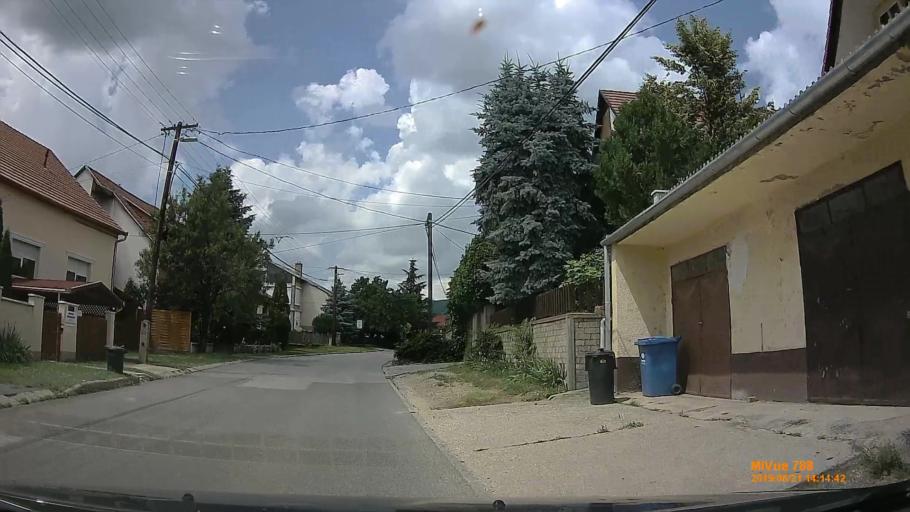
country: HU
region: Baranya
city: Pecs
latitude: 46.0810
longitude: 18.1855
